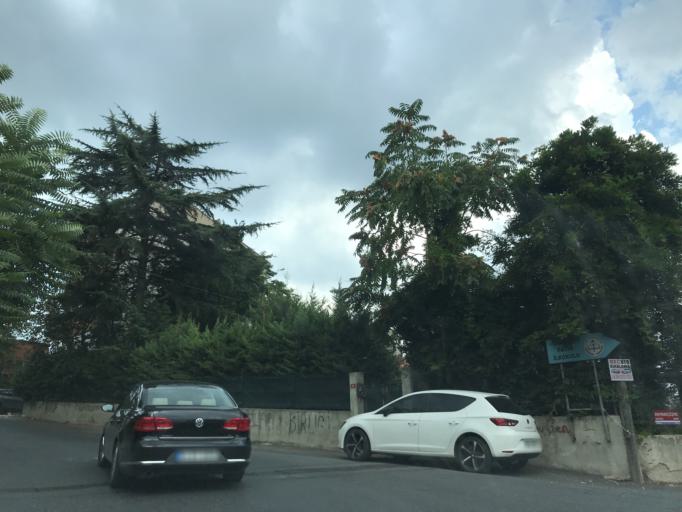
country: TR
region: Istanbul
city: Arikoey
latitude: 41.1773
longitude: 29.0522
